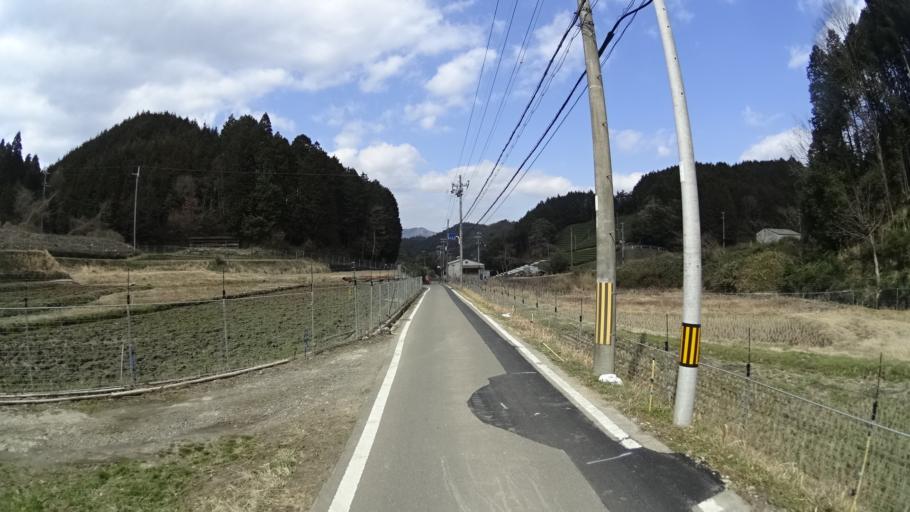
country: JP
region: Nara
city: Nara-shi
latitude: 34.7795
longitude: 135.9076
